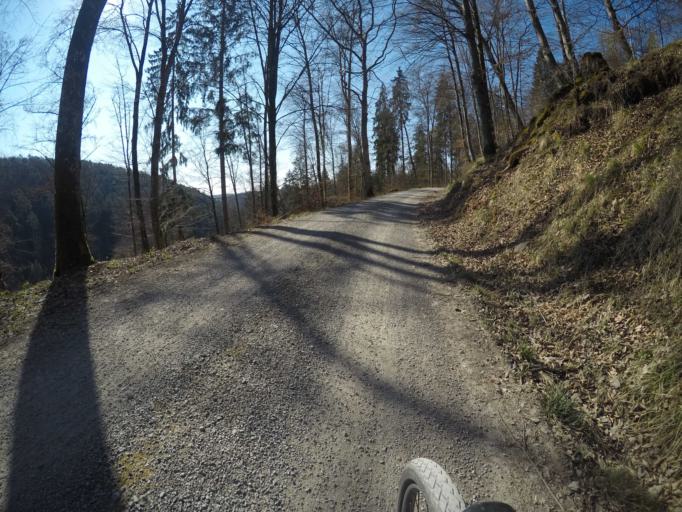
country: DE
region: Baden-Wuerttemberg
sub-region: Tuebingen Region
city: Tuebingen
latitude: 48.5691
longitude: 9.0309
